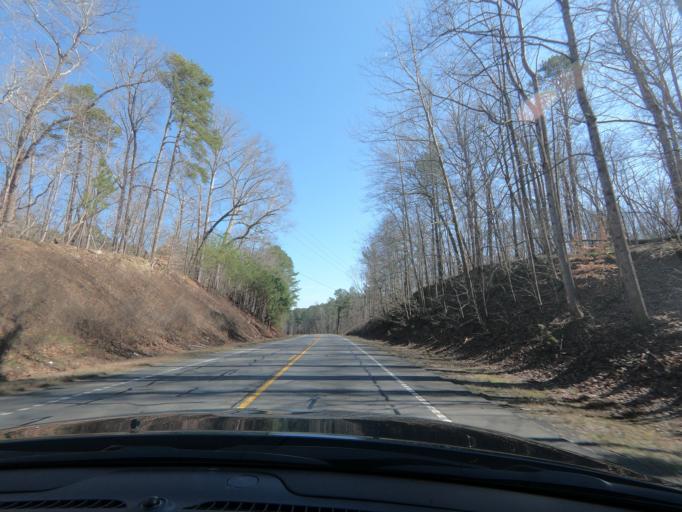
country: US
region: Georgia
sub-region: Forsyth County
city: Cumming
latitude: 34.3025
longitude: -84.2228
